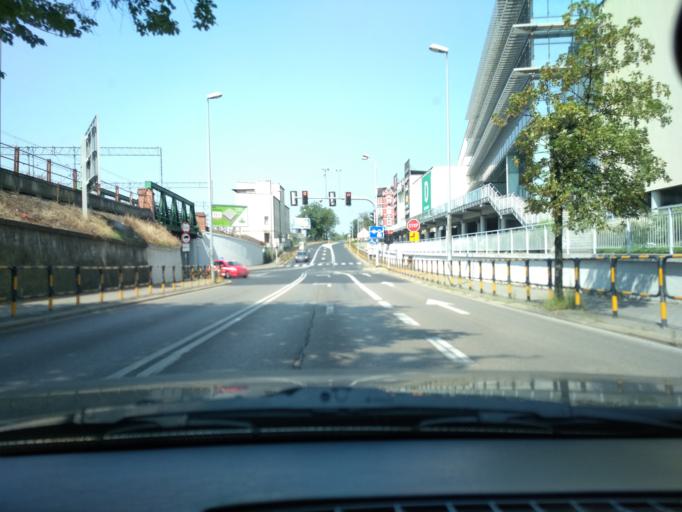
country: PL
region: Silesian Voivodeship
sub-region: Gliwice
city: Gliwice
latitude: 50.2995
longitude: 18.6823
